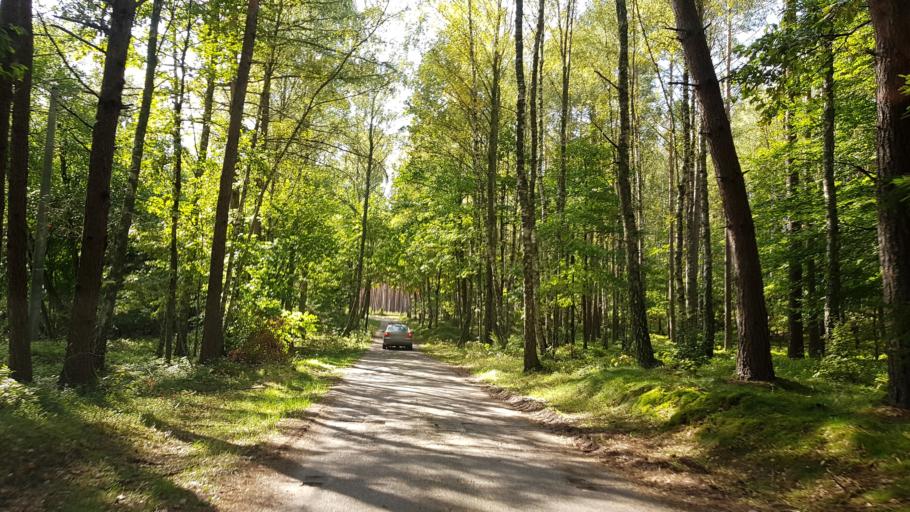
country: PL
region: West Pomeranian Voivodeship
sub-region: Powiat koszalinski
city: Bobolice
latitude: 54.0542
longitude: 16.5927
